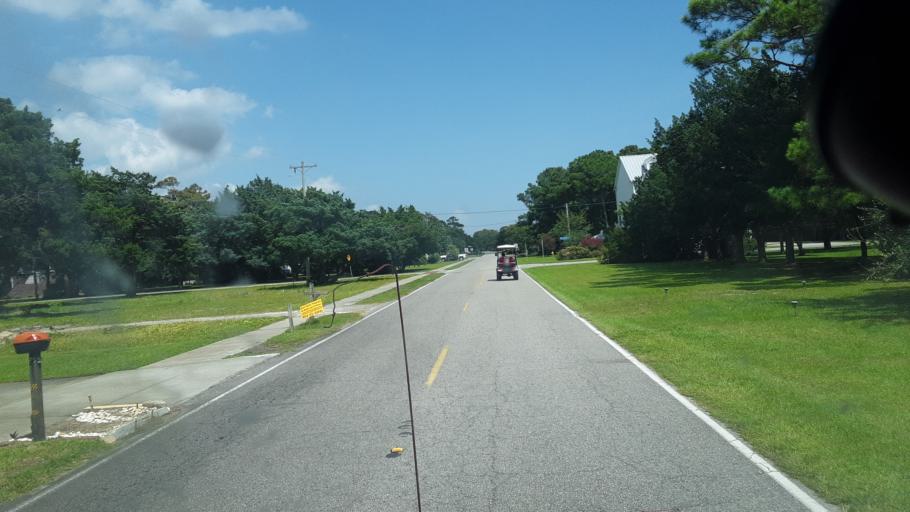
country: US
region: South Carolina
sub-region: Horry County
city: North Myrtle Beach
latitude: 33.8240
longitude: -78.6622
